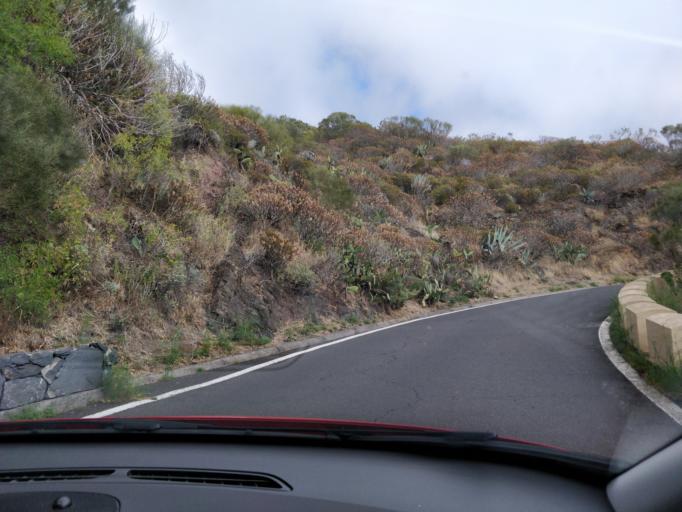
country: ES
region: Canary Islands
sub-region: Provincia de Santa Cruz de Tenerife
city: Santiago del Teide
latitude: 28.3175
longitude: -16.8523
